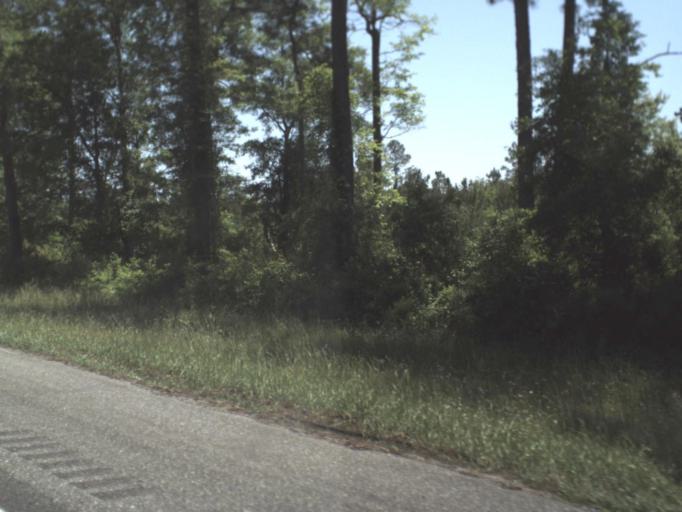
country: US
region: Florida
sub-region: Jefferson County
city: Monticello
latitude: 30.4616
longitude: -83.7846
